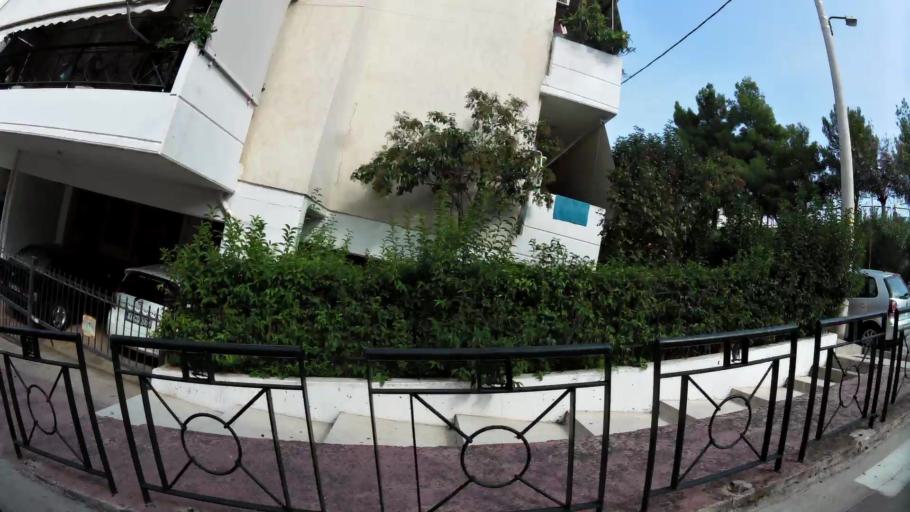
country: GR
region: Attica
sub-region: Nomarchia Athinas
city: Galatsi
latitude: 38.0117
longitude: 23.7594
